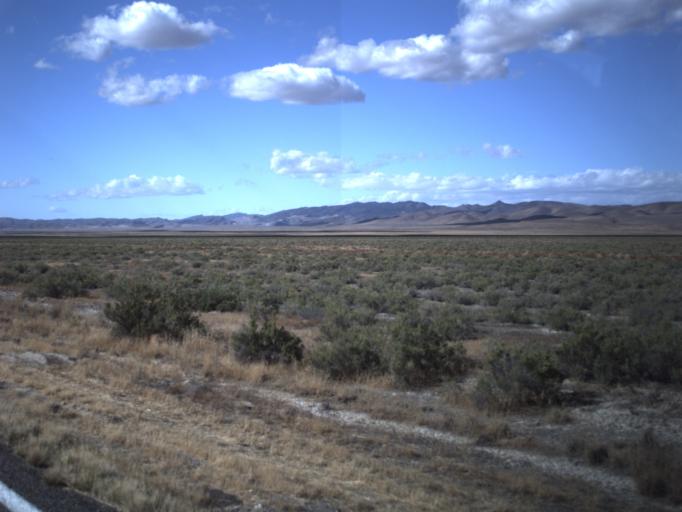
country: US
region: Utah
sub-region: Millard County
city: Delta
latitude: 39.0655
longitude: -112.7615
